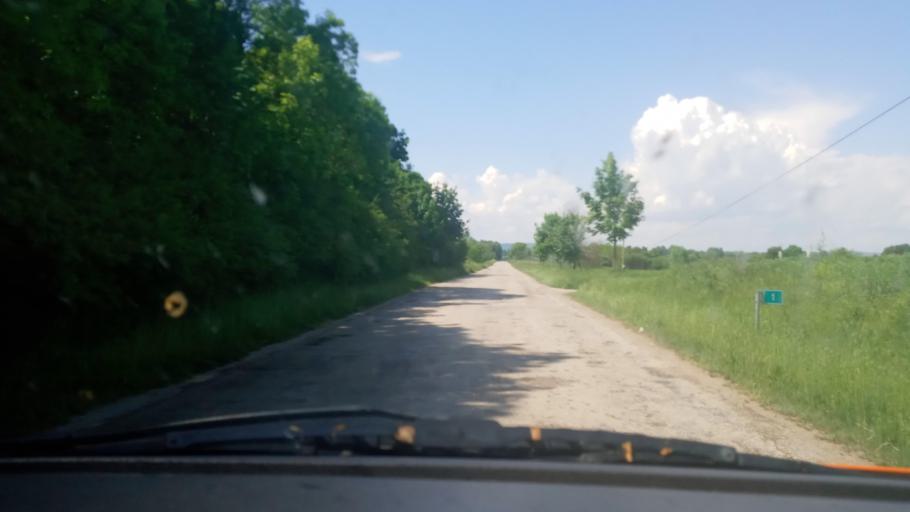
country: HU
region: Baranya
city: Siklos
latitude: 45.8042
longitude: 18.3449
